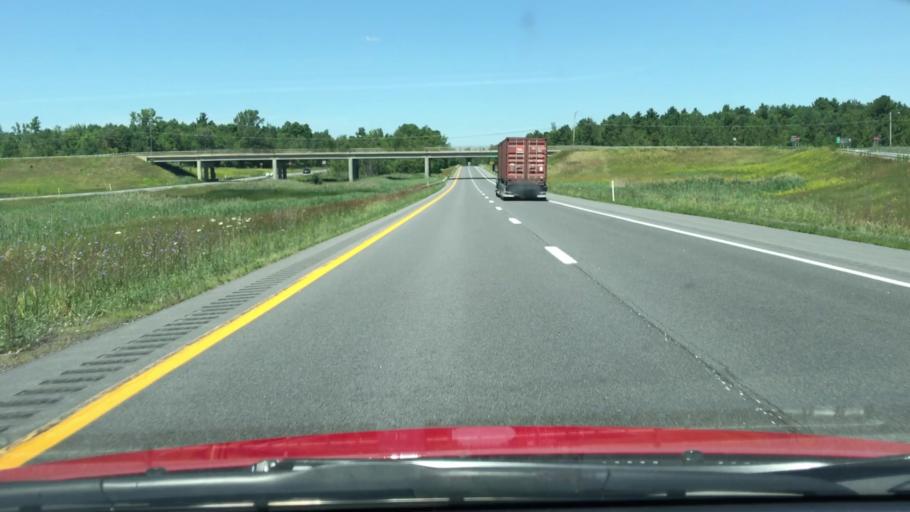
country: US
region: New York
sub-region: Clinton County
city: Champlain
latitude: 44.8879
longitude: -73.4525
